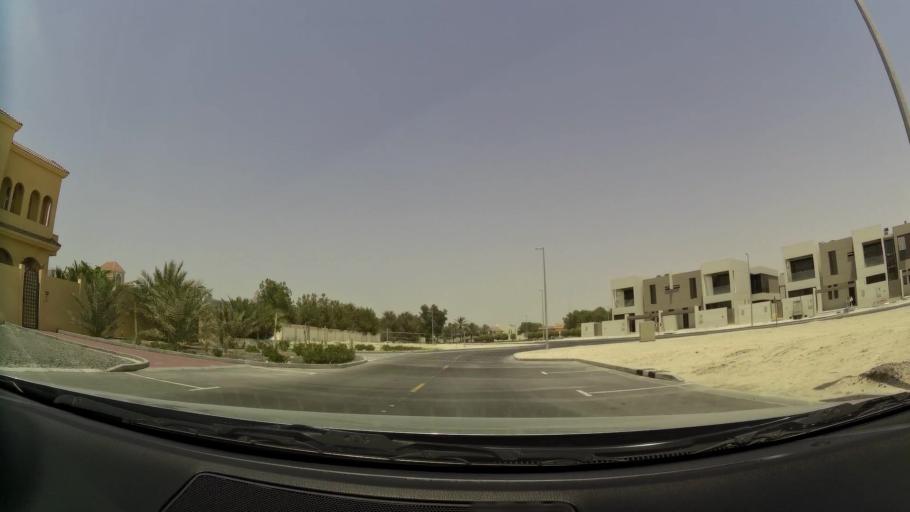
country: AE
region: Dubai
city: Dubai
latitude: 25.1334
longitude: 55.1976
